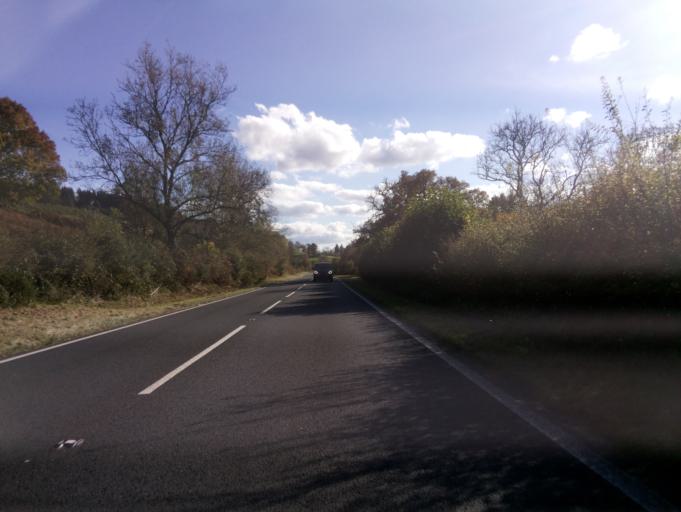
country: GB
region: Wales
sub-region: Merthyr Tydfil County Borough
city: Merthyr Tydfil
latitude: 51.8190
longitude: -3.4441
